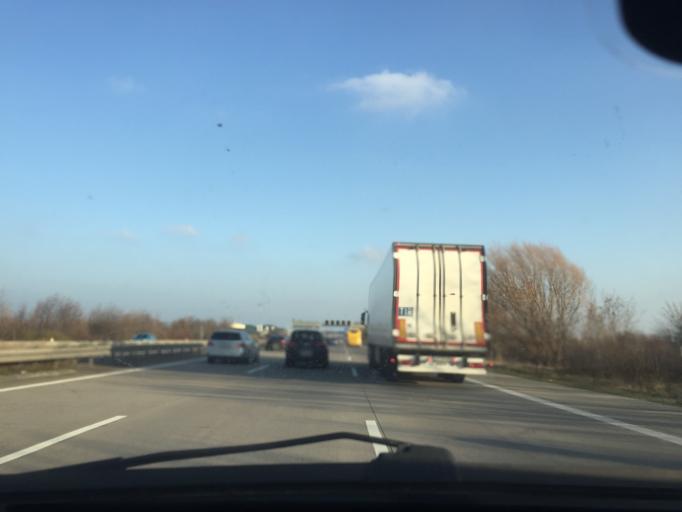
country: DE
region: Saxony-Anhalt
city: Ebendorf
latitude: 52.1708
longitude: 11.5592
